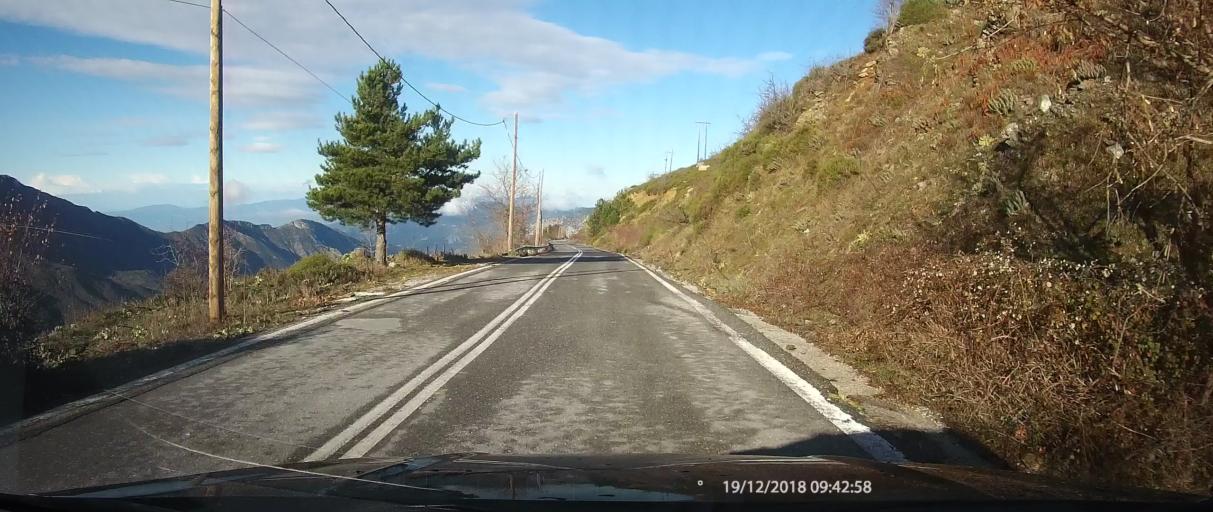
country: GR
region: Peloponnese
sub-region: Nomos Messinias
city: Paralia Vergas
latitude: 37.0698
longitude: 22.2611
